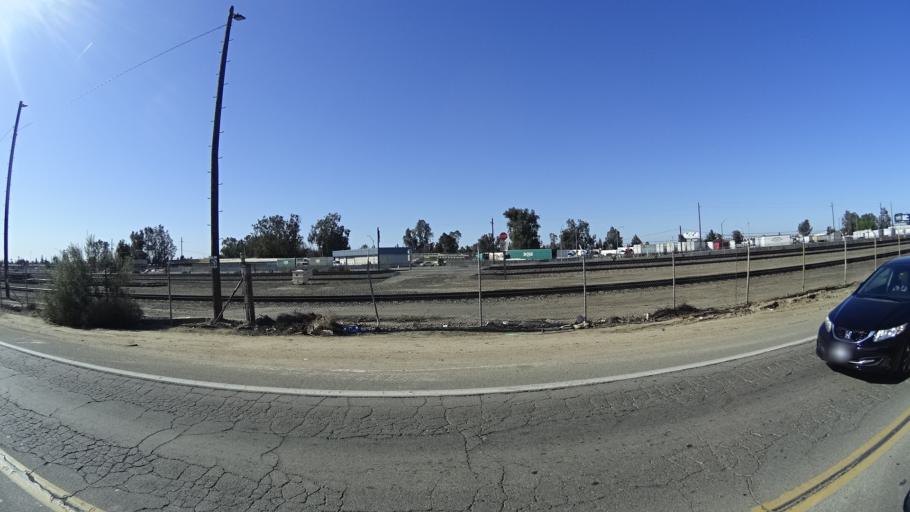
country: US
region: California
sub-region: Fresno County
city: West Park
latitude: 36.7930
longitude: -119.8593
